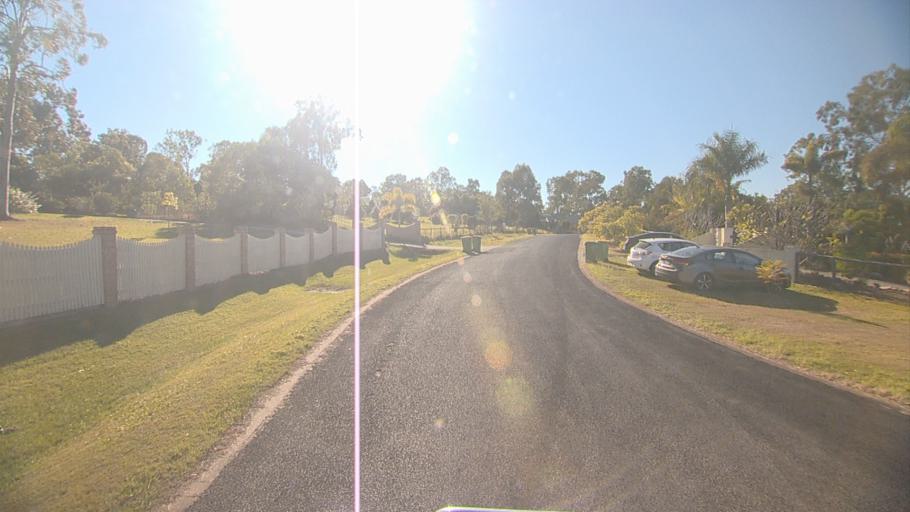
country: AU
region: Queensland
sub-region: Logan
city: North Maclean
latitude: -27.7449
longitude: 152.9602
